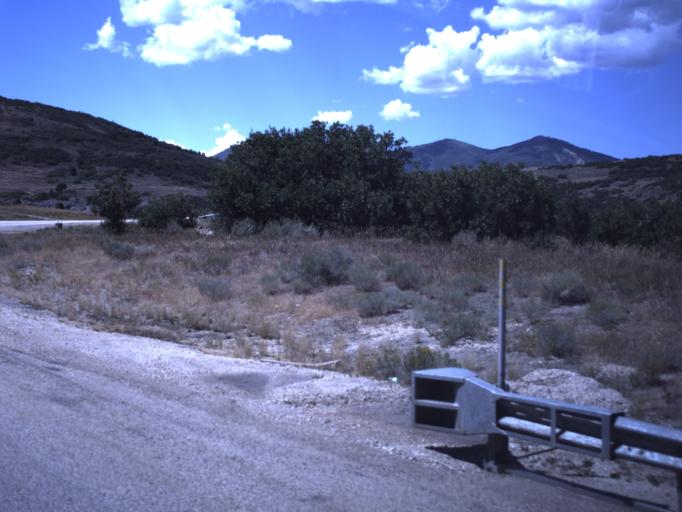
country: US
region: Utah
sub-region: Wasatch County
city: Heber
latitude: 40.5903
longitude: -111.3783
